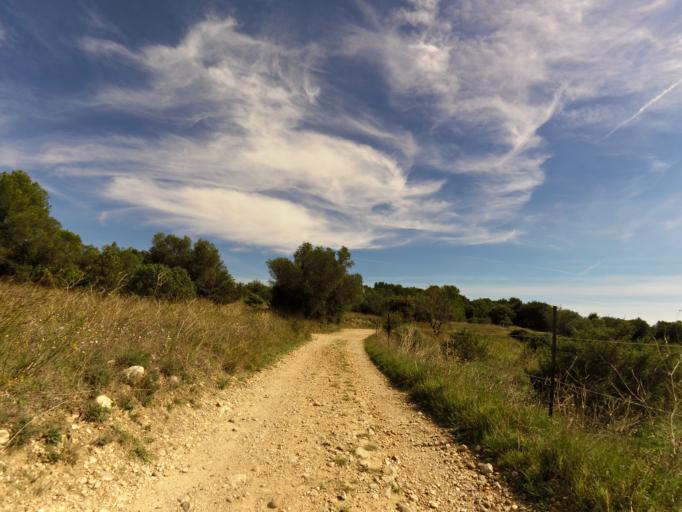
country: FR
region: Languedoc-Roussillon
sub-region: Departement du Gard
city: Mus
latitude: 43.7471
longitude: 4.1963
